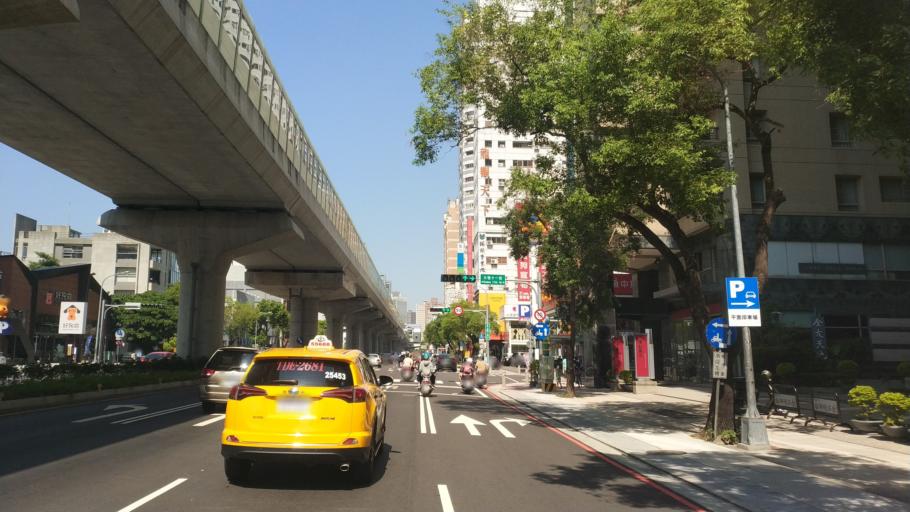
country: TW
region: Taiwan
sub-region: Taichung City
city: Taichung
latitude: 24.1484
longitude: 120.6468
